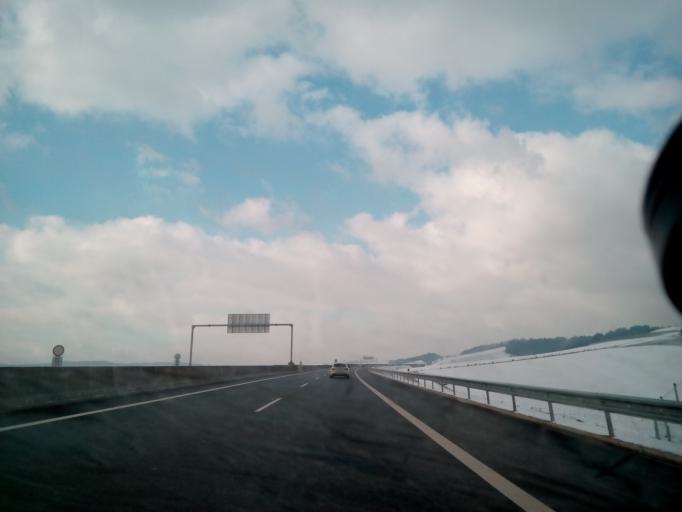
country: SK
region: Presovsky
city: Spisske Podhradie
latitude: 49.0065
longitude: 20.6919
